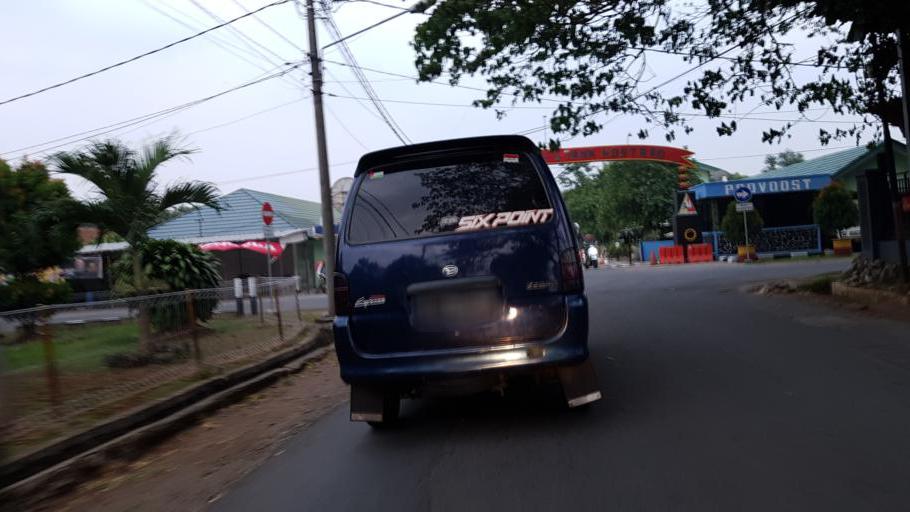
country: ID
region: West Java
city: Depok
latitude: -6.3387
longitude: 106.8439
